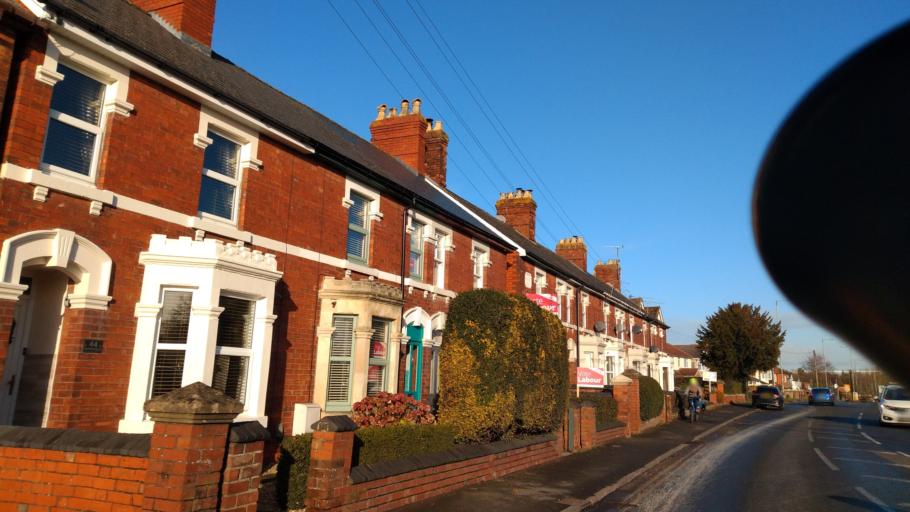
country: GB
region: England
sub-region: Borough of Swindon
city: Broad Blunsdon
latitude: 51.5866
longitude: -1.7498
